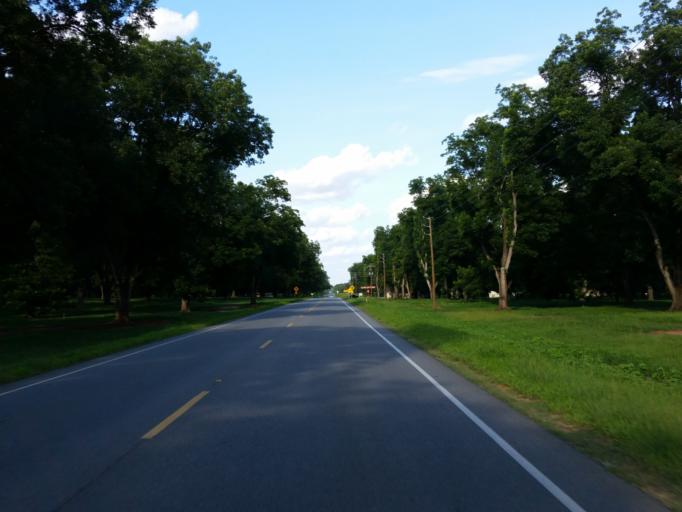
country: US
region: Georgia
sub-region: Crisp County
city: Cordele
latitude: 31.9608
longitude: -83.9580
